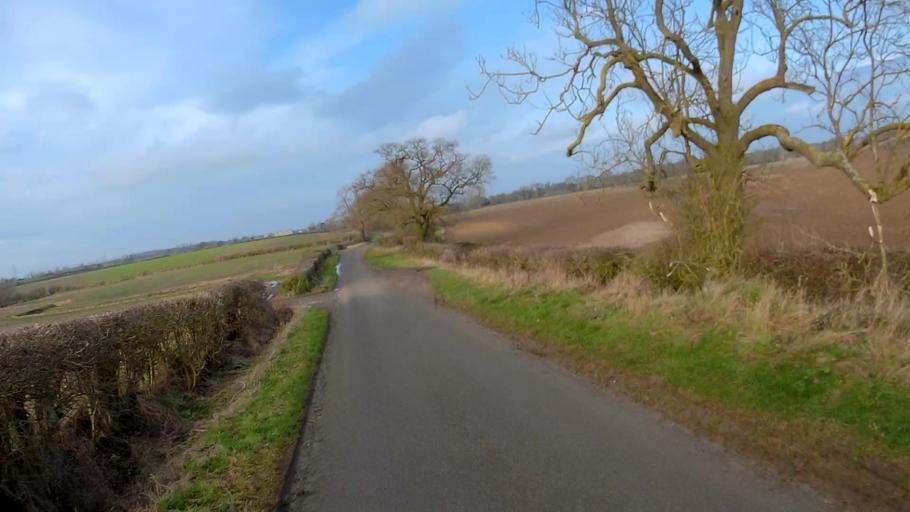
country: GB
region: England
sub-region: Lincolnshire
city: Bourne
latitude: 52.7701
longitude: -0.4237
